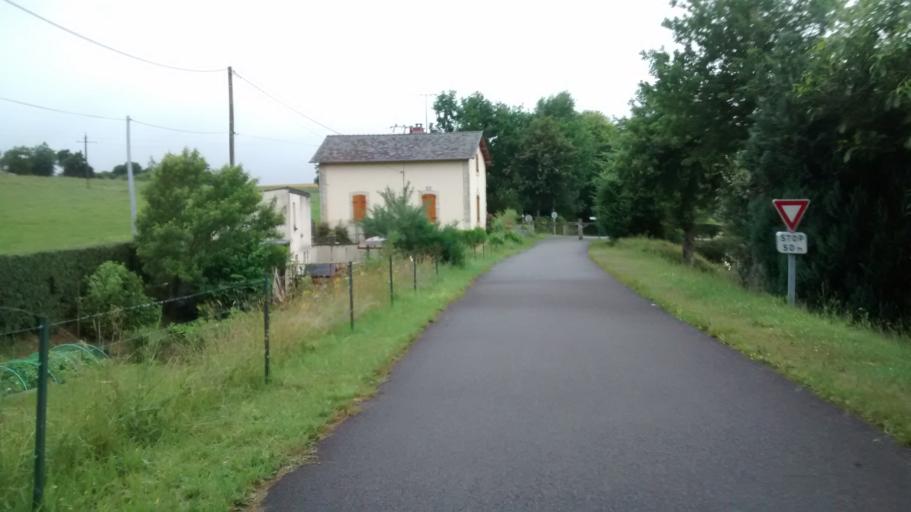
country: FR
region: Brittany
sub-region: Departement du Morbihan
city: Pleucadeuc
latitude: 47.7736
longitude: -2.3982
